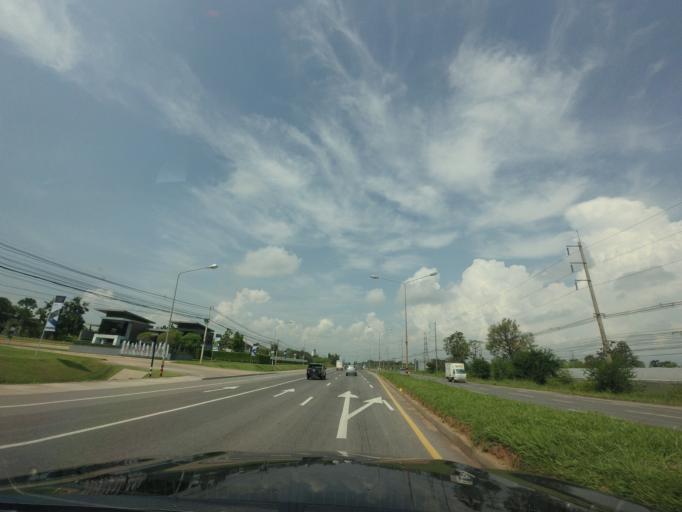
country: TH
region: Khon Kaen
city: Khon Kaen
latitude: 16.4508
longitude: 102.7485
